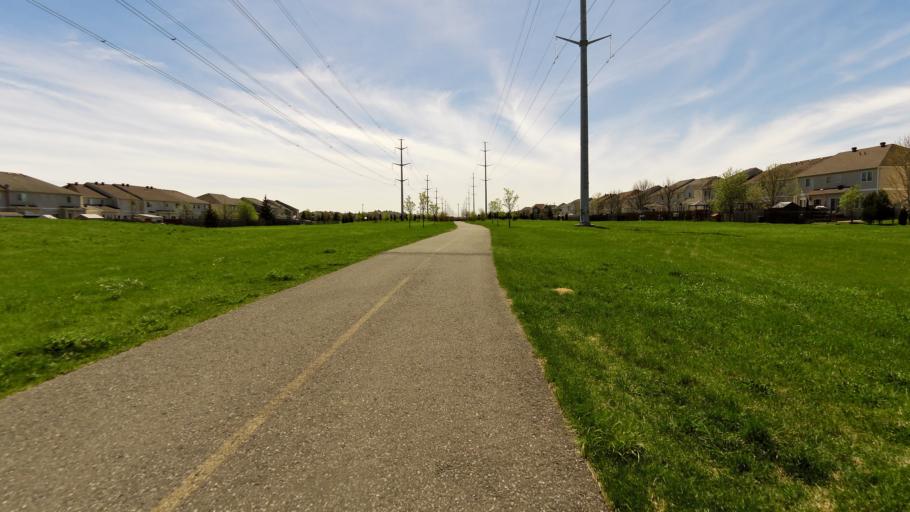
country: CA
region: Ontario
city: Clarence-Rockland
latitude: 45.4741
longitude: -75.4624
